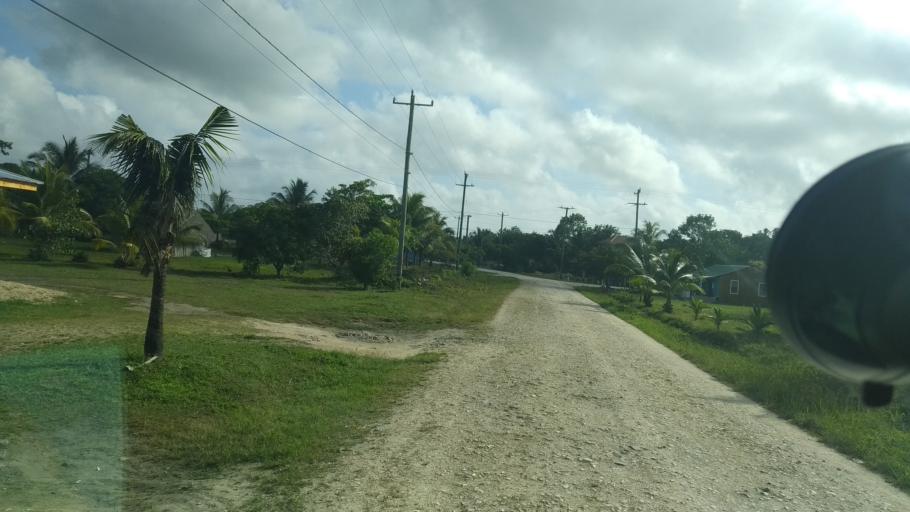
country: BZ
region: Stann Creek
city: Placencia
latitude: 16.5093
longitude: -88.5466
